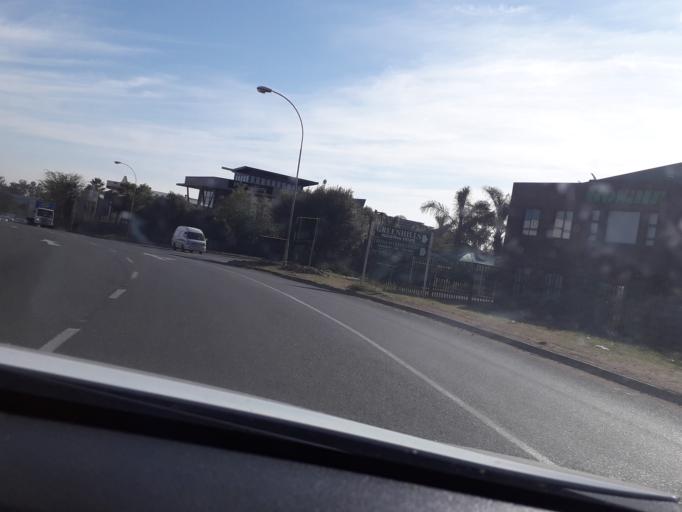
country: ZA
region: Gauteng
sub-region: Ekurhuleni Metropolitan Municipality
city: Germiston
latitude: -26.1628
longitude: 28.1813
